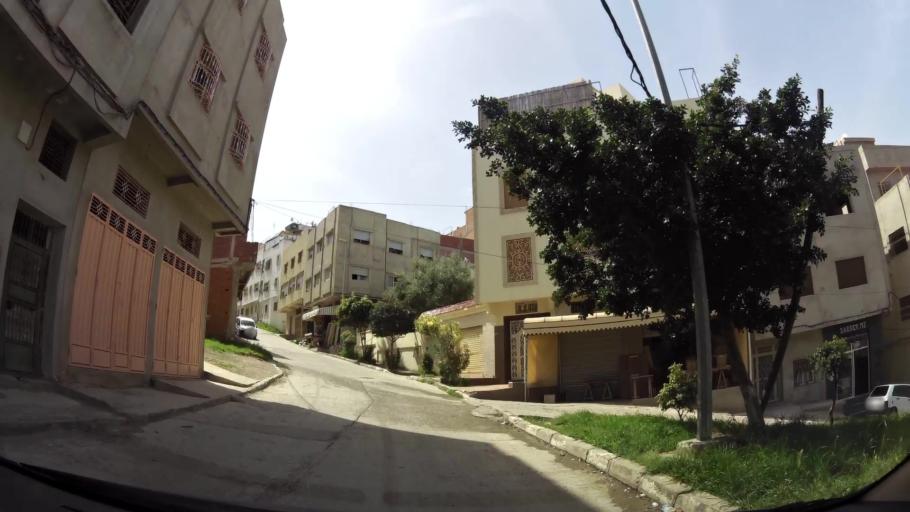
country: MA
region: Tanger-Tetouan
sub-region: Tanger-Assilah
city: Tangier
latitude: 35.7475
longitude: -5.8307
